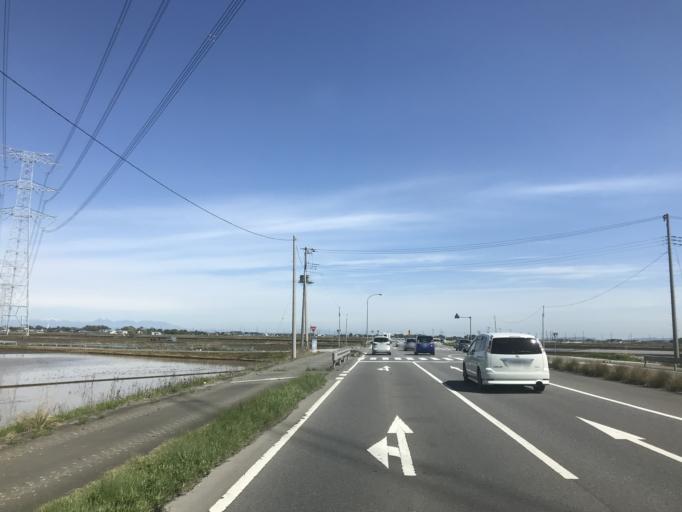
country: JP
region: Ibaraki
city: Ishige
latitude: 36.1254
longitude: 139.9821
